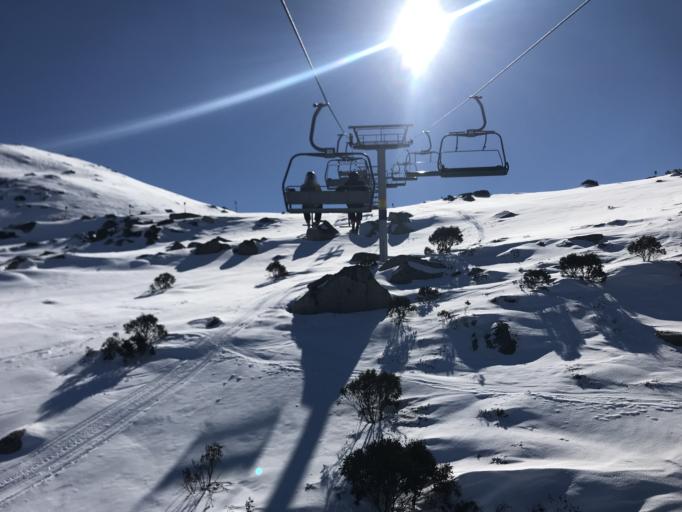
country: AU
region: New South Wales
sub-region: Snowy River
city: Jindabyne
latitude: -36.3801
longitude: 148.3966
